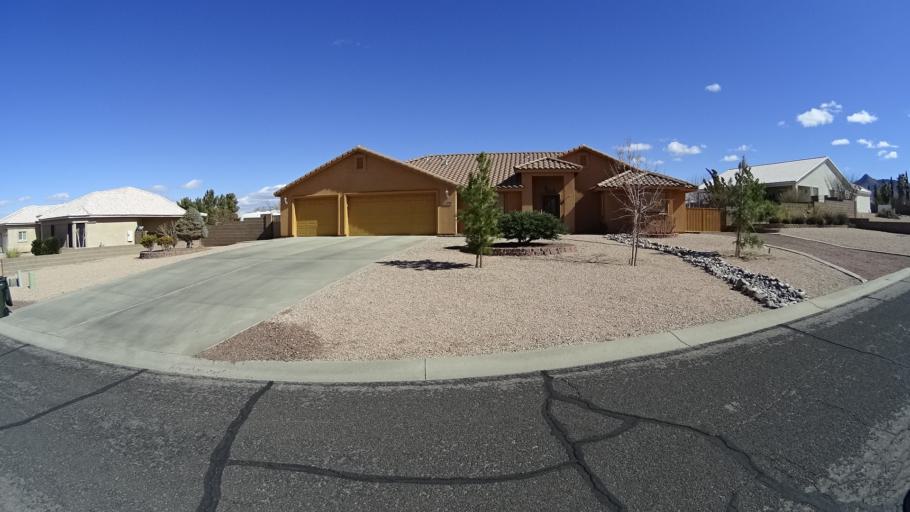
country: US
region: Arizona
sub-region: Mohave County
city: Kingman
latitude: 35.2076
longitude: -113.9753
